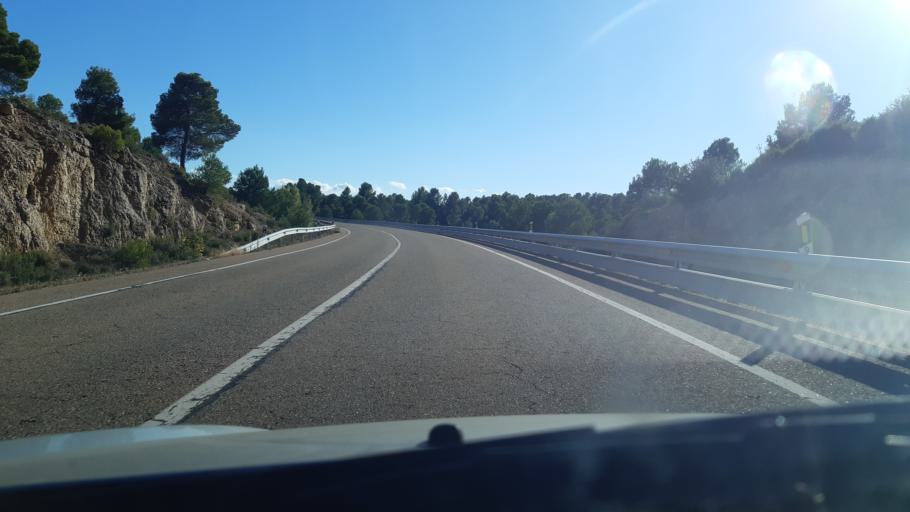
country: ES
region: Aragon
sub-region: Provincia de Teruel
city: Fornoles
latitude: 40.9237
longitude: -0.0193
